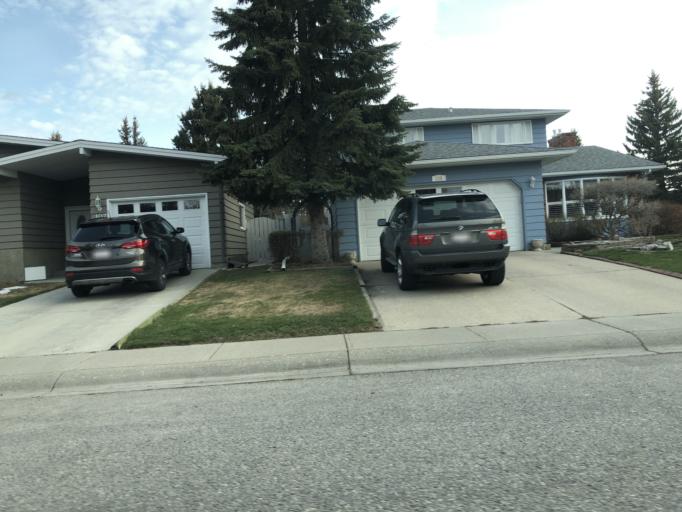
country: CA
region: Alberta
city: Calgary
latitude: 50.9309
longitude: -114.0449
